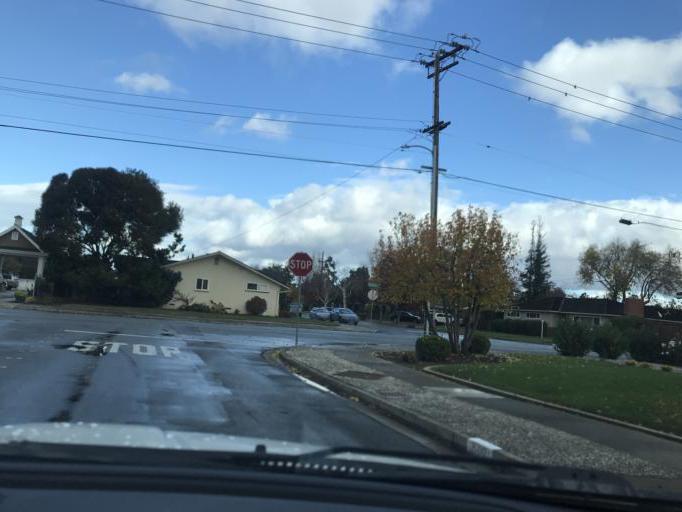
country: US
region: California
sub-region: Santa Clara County
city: Buena Vista
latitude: 37.2978
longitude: -121.9150
